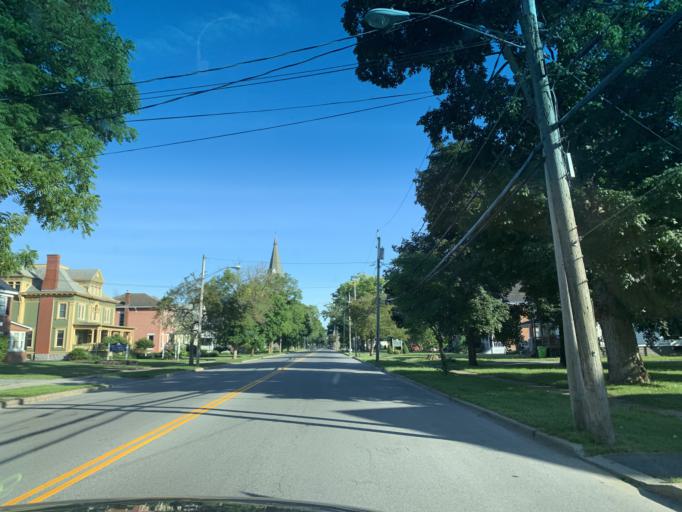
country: US
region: New York
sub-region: Madison County
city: Oneida
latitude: 43.0911
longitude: -75.6496
